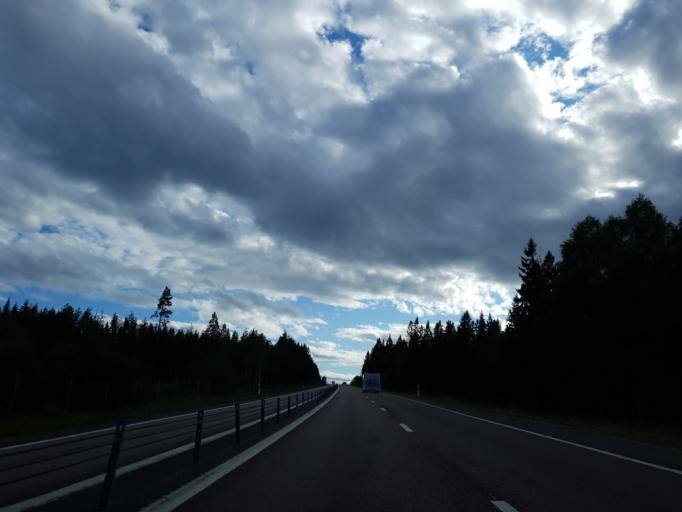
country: SE
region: Vaesternorrland
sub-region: Haernoesands Kommun
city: Haernoesand
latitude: 62.5743
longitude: 17.7483
